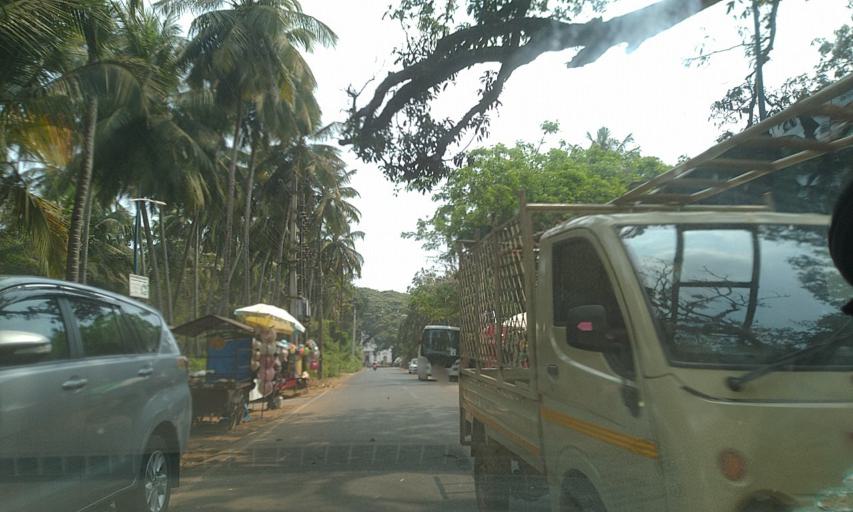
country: IN
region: Goa
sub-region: North Goa
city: Jua
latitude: 15.5047
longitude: 73.9122
